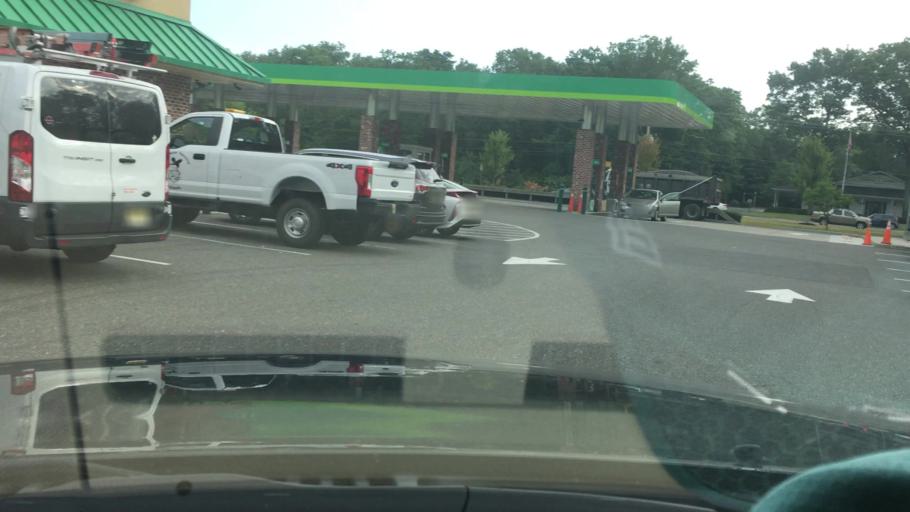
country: US
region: New Jersey
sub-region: Ocean County
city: Leisure Village West-Pine Lake Park
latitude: 40.0235
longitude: -74.2716
